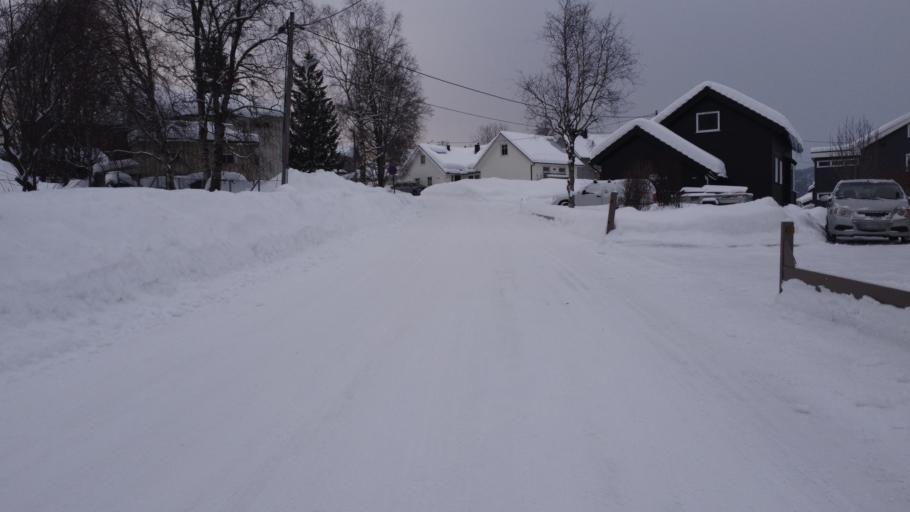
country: NO
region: Nordland
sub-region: Rana
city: Mo i Rana
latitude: 66.3156
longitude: 14.1471
